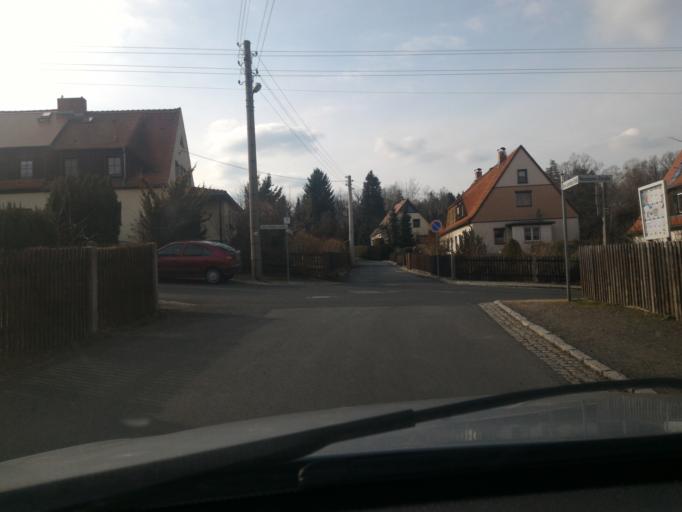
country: DE
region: Saxony
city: Olbersdorf
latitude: 50.8670
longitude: 14.7563
